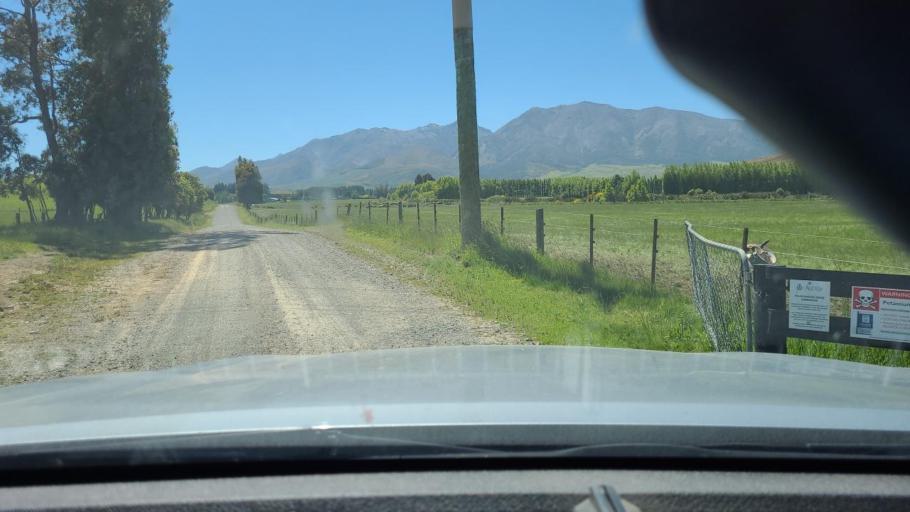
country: NZ
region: Southland
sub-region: Southland District
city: Te Anau
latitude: -45.8459
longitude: 167.7112
